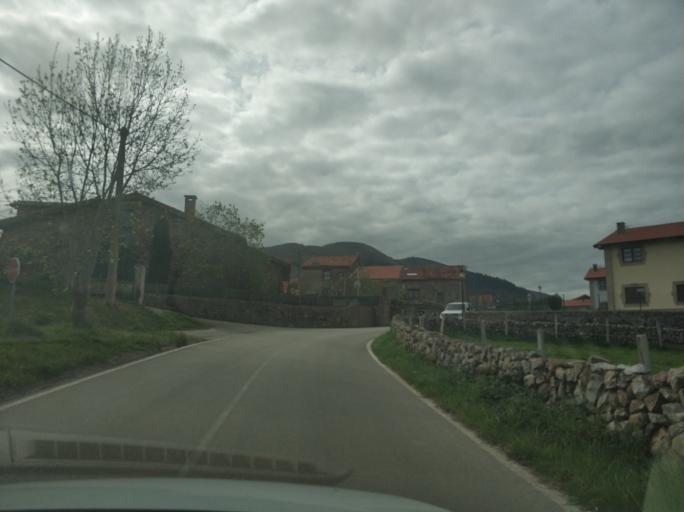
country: ES
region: Cantabria
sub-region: Provincia de Cantabria
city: Ruente
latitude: 43.2350
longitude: -4.2821
